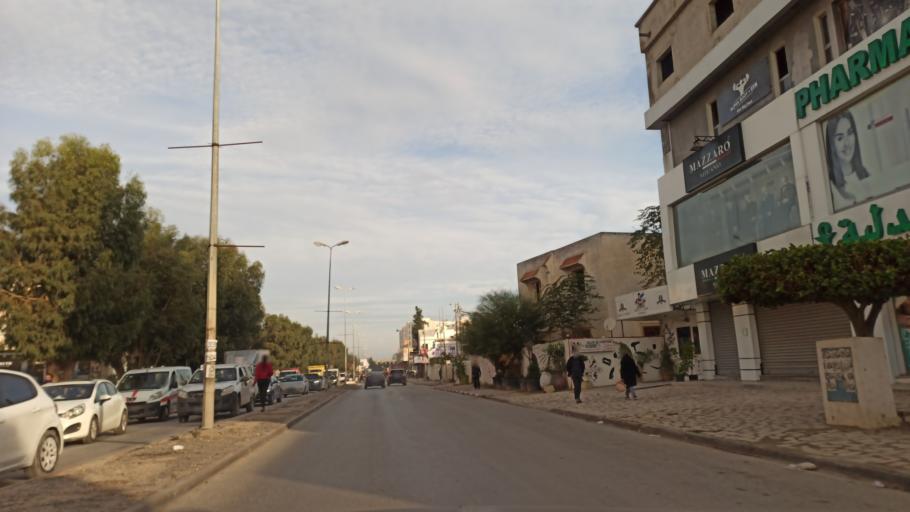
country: TN
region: Tunis
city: La Goulette
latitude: 36.8555
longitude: 10.2571
